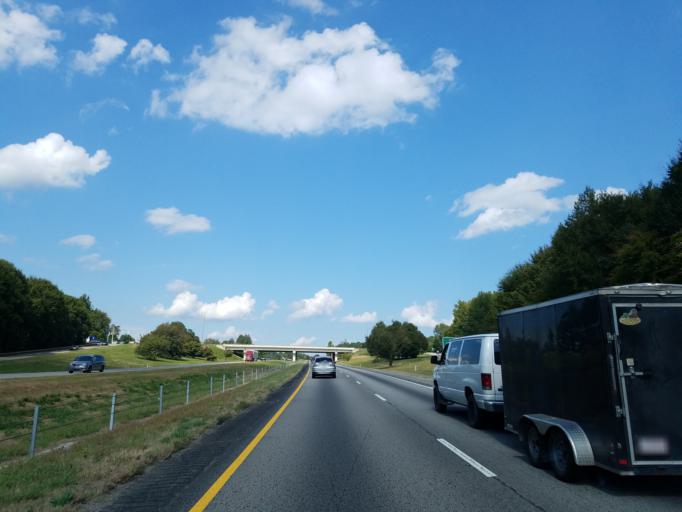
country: US
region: Georgia
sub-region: Jackson County
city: Jefferson
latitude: 34.1499
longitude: -83.6488
